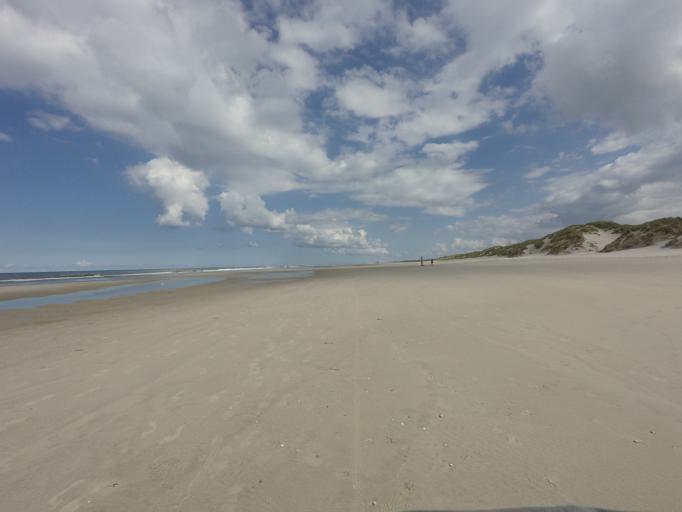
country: NL
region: Friesland
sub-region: Gemeente Terschelling
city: West-Terschelling
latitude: 53.4006
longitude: 5.2327
